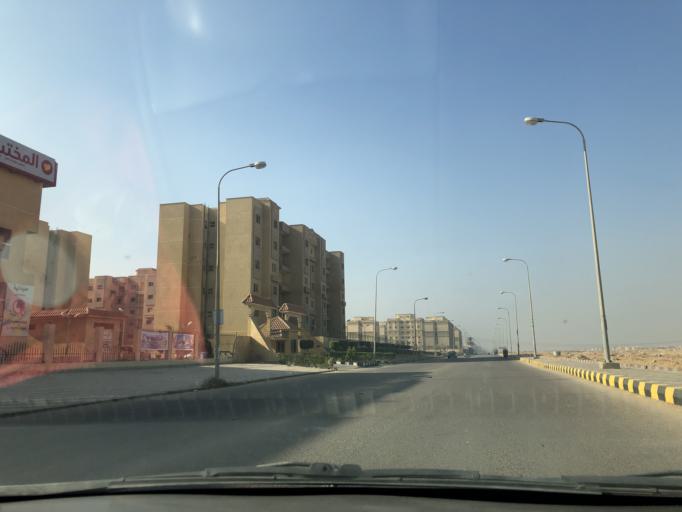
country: EG
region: Al Jizah
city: Madinat Sittah Uktubar
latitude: 29.9176
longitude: 31.0596
